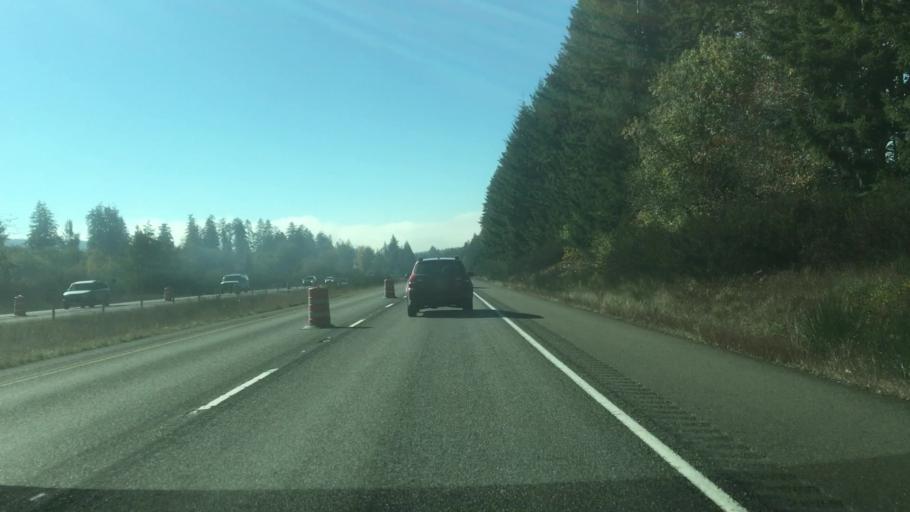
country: US
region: Washington
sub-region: Grays Harbor County
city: McCleary
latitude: 47.0516
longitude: -123.2973
